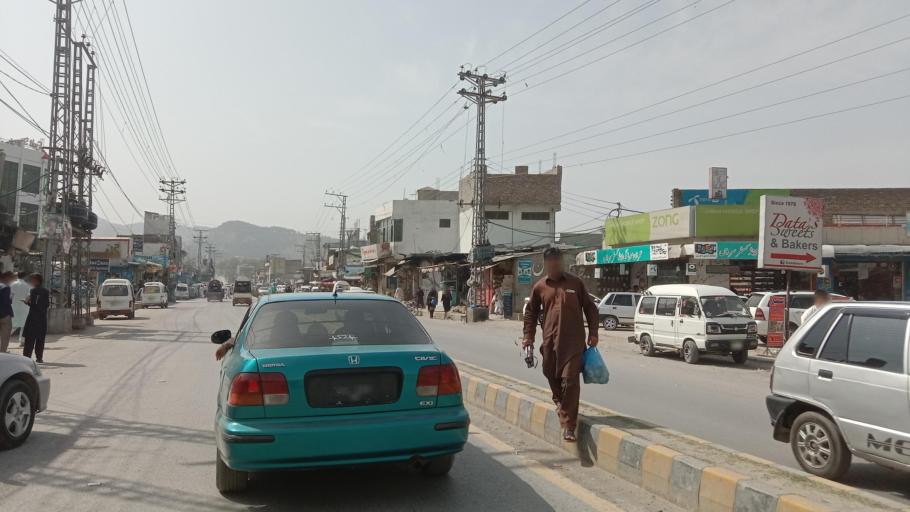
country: PK
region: Khyber Pakhtunkhwa
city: Abbottabad
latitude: 34.1571
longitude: 73.2363
